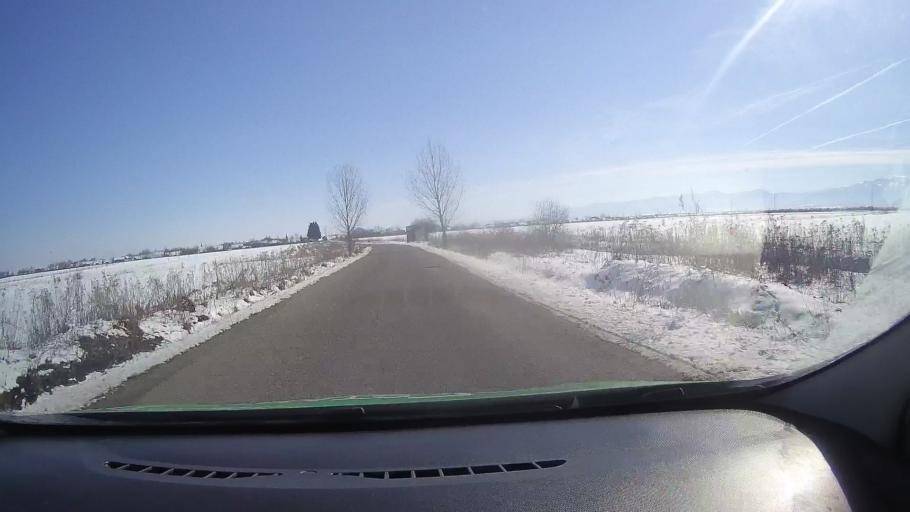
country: RO
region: Brasov
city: Fogarasch
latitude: 45.8172
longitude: 24.9948
